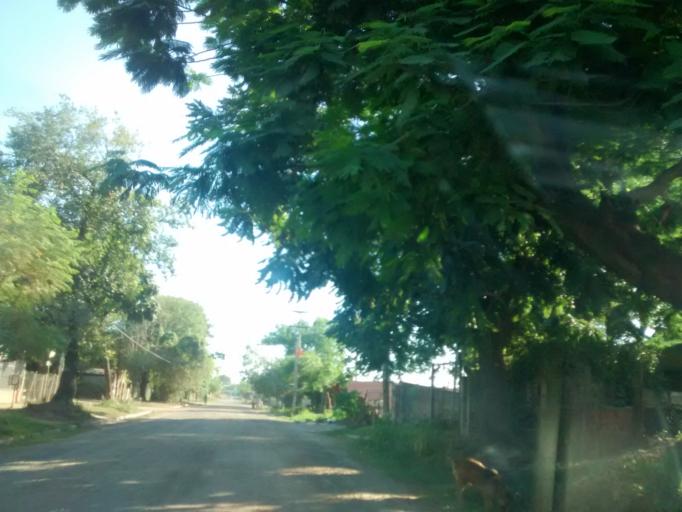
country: AR
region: Chaco
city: Resistencia
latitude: -27.4615
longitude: -58.9620
